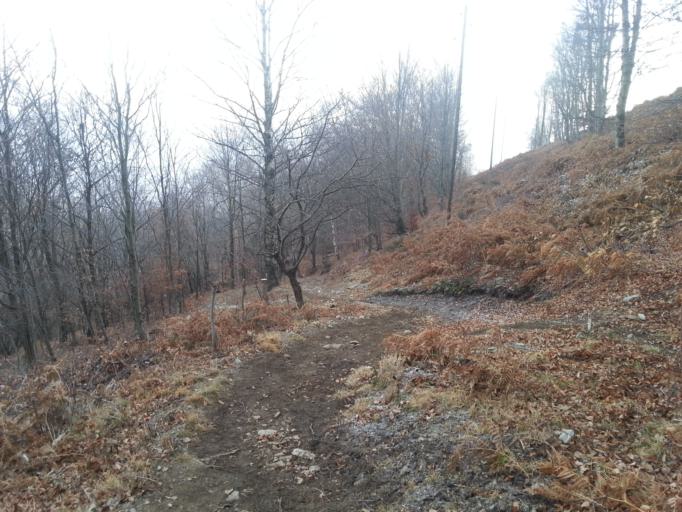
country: CH
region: Ticino
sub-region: Lugano District
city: Pura
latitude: 46.0314
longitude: 8.8469
